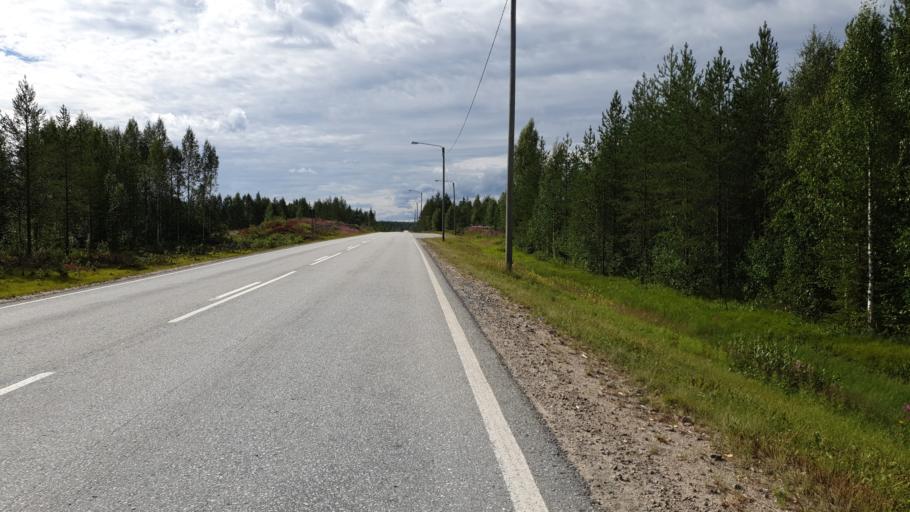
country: FI
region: Kainuu
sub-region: Kehys-Kainuu
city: Kuhmo
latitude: 64.5339
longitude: 29.9441
